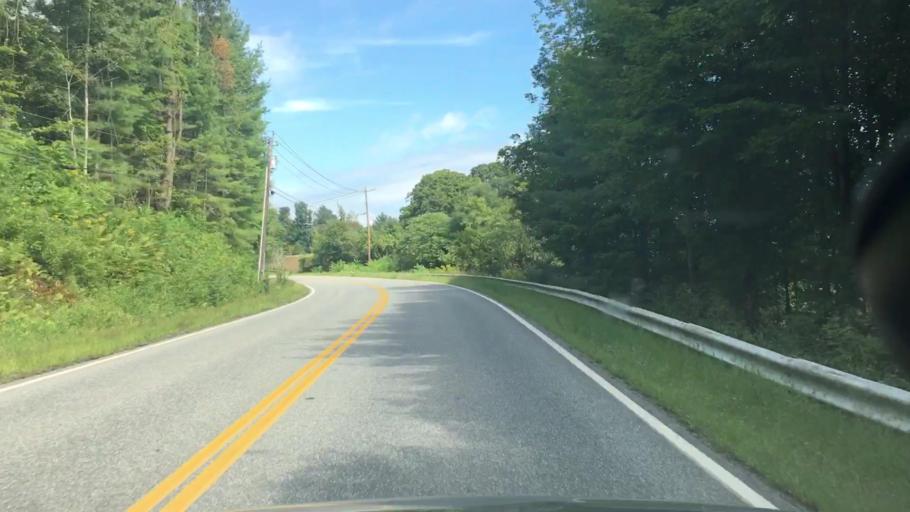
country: US
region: Massachusetts
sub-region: Franklin County
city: Colrain
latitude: 42.6374
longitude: -72.6689
